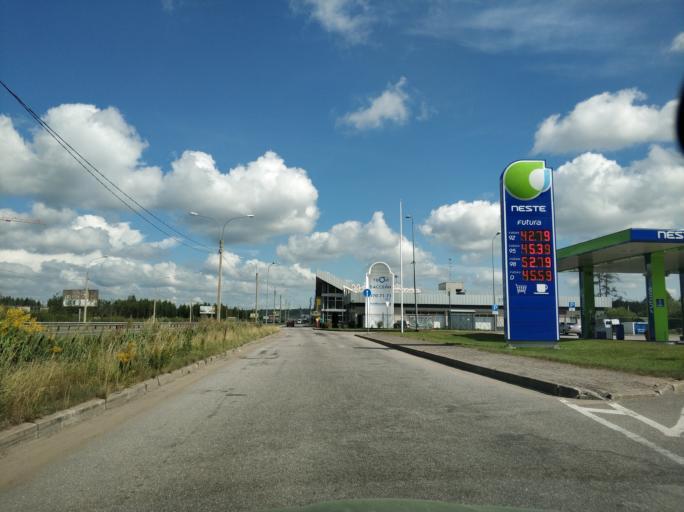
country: RU
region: Leningrad
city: Vsevolozhsk
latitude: 60.0202
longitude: 30.6009
